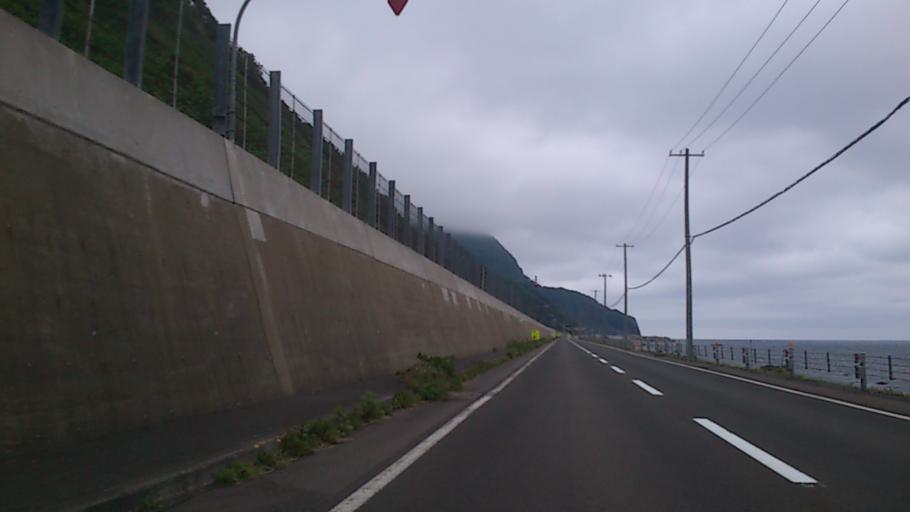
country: JP
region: Hokkaido
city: Iwanai
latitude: 42.6788
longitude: 139.8973
